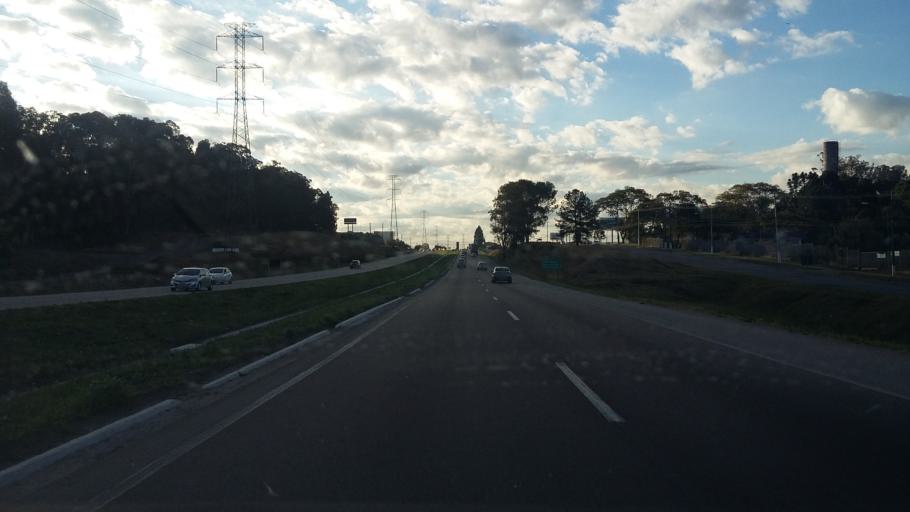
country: BR
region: Parana
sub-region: Curitiba
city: Curitiba
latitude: -25.4622
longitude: -49.3581
